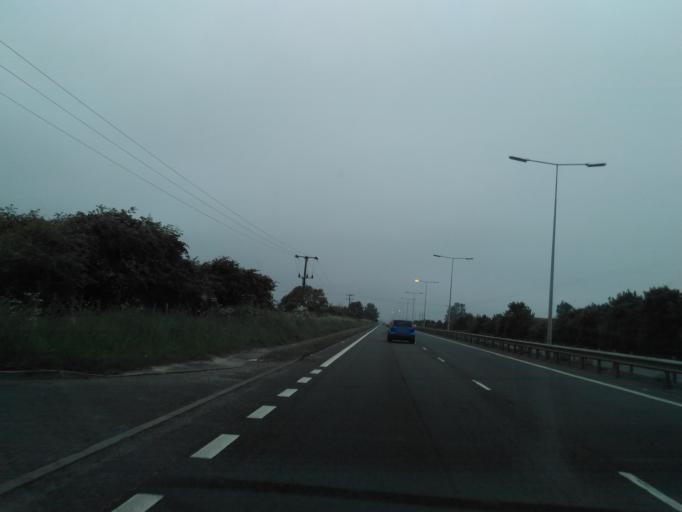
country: GB
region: England
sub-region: Kent
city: Dunkirk
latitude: 51.3297
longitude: 0.9954
